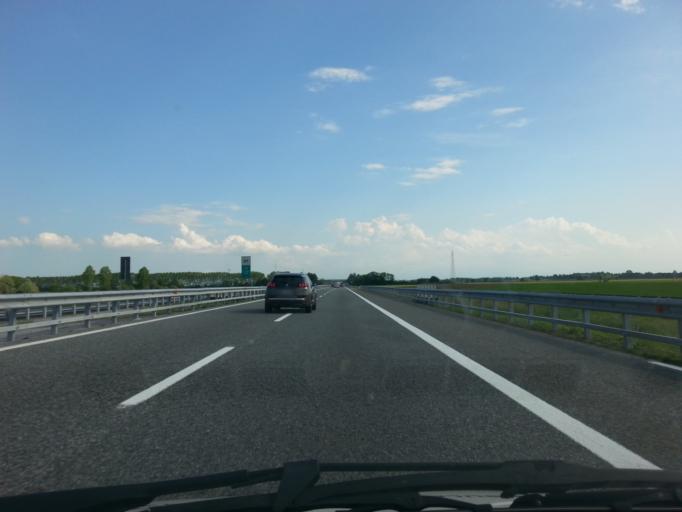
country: IT
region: Piedmont
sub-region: Provincia di Cuneo
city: Sommariva del Bosco
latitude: 44.7293
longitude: 7.7557
